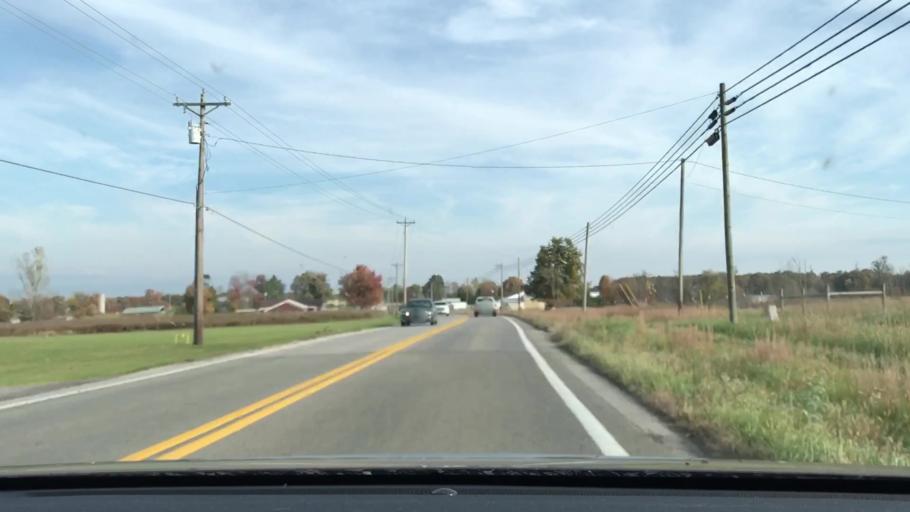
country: US
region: Tennessee
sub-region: Fentress County
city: Grimsley
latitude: 36.2130
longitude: -85.0145
